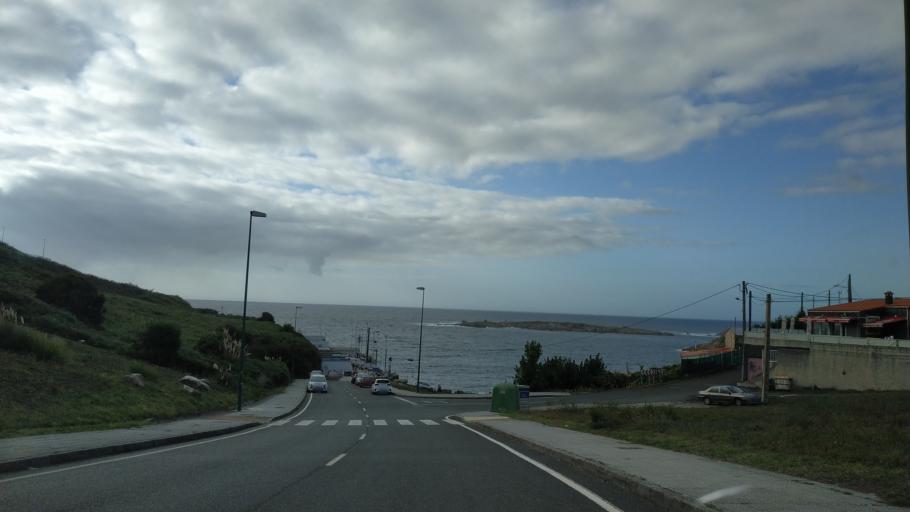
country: ES
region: Galicia
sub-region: Provincia da Coruna
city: A Coruna
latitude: 43.3717
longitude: -8.4452
